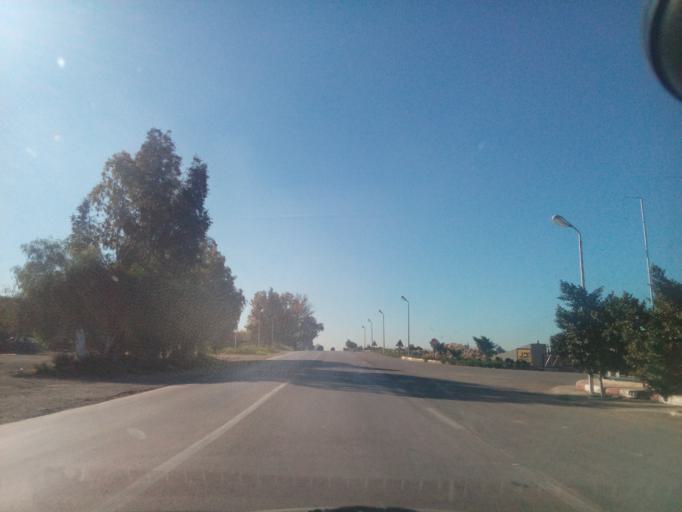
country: DZ
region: Relizane
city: Oued Rhiou
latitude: 35.9861
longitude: 0.9719
